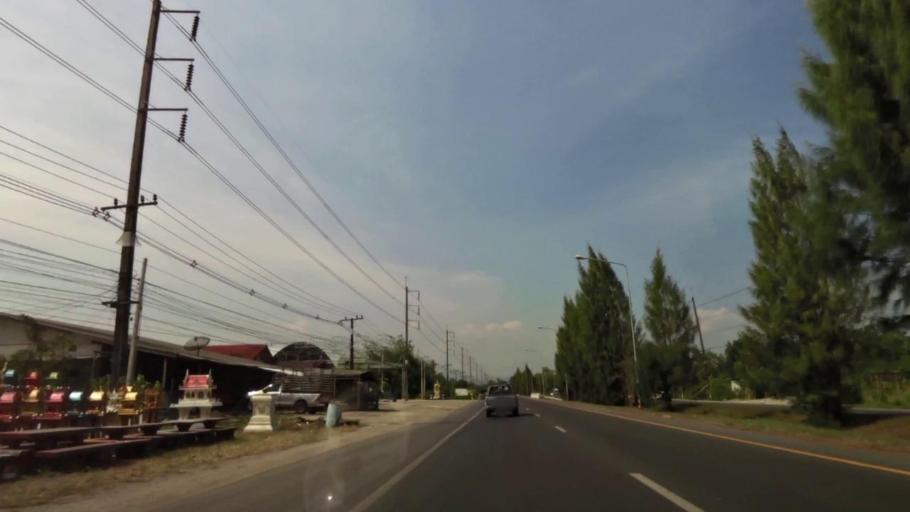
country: TH
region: Chanthaburi
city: Chanthaburi
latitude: 12.6386
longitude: 102.1354
